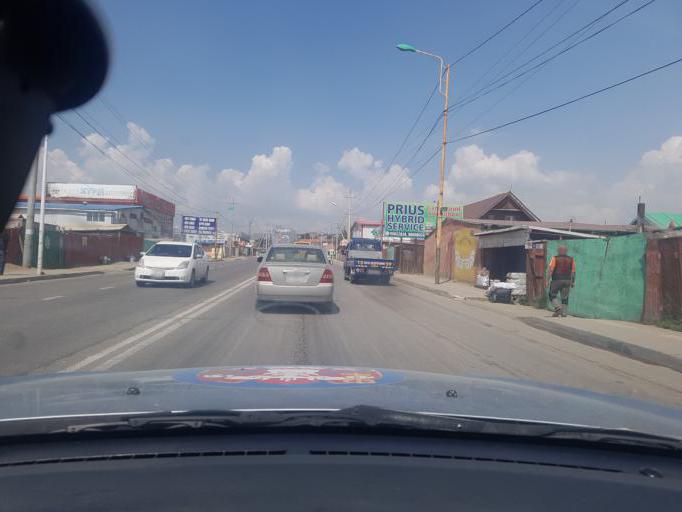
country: MN
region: Ulaanbaatar
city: Ulaanbaatar
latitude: 47.9314
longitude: 106.8879
